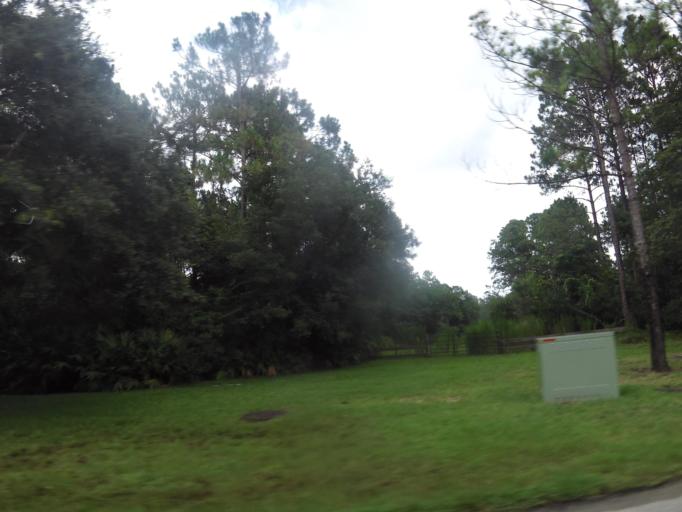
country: US
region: Florida
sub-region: Saint Johns County
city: Ponte Vedra Beach
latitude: 30.2522
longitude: -81.4368
